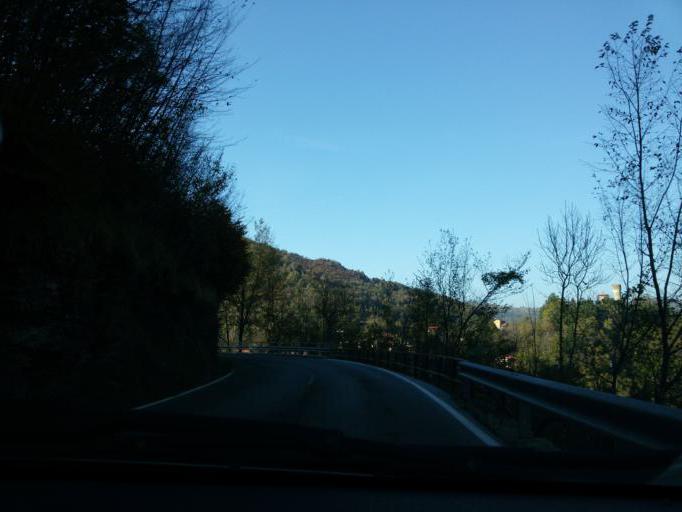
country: IT
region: Liguria
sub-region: Provincia di Genova
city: Ferriere
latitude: 44.4831
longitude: 9.1259
